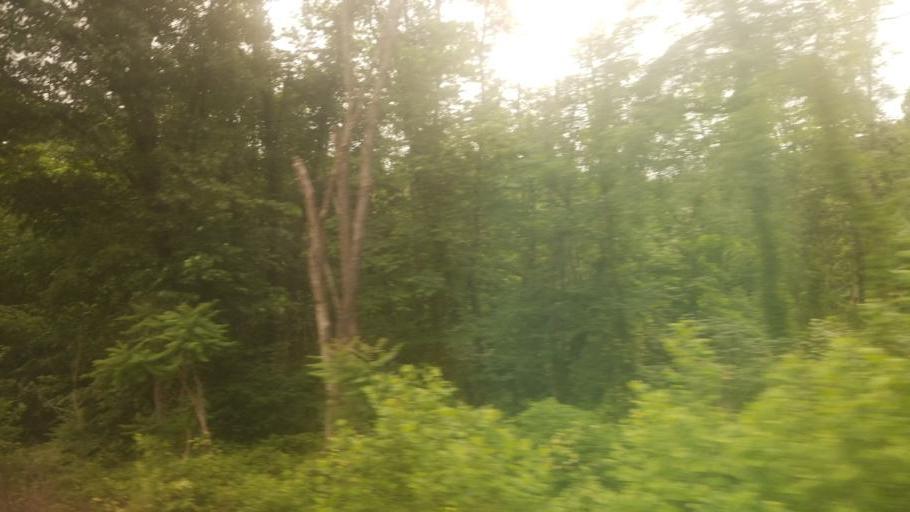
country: US
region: West Virginia
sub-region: Morgan County
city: Berkeley Springs
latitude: 39.5782
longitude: -78.4018
